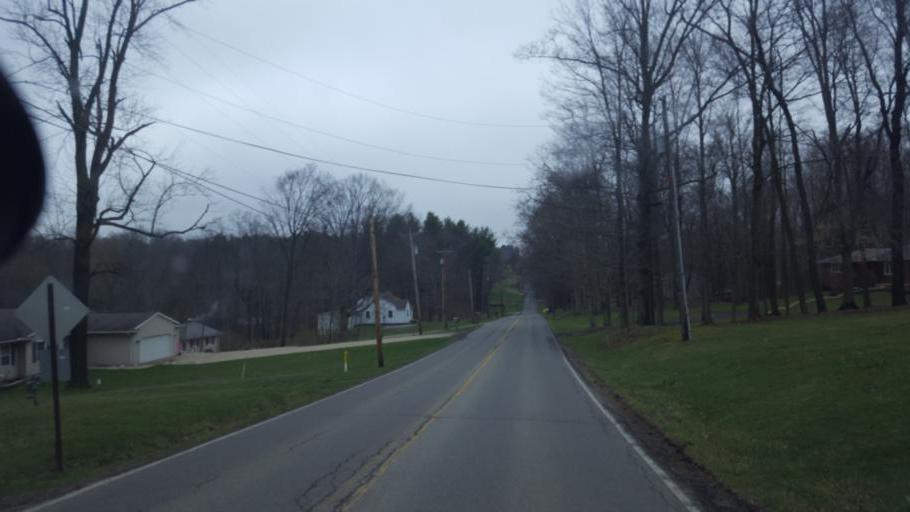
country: US
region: Ohio
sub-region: Richland County
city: Lexington
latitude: 40.6960
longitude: -82.5561
